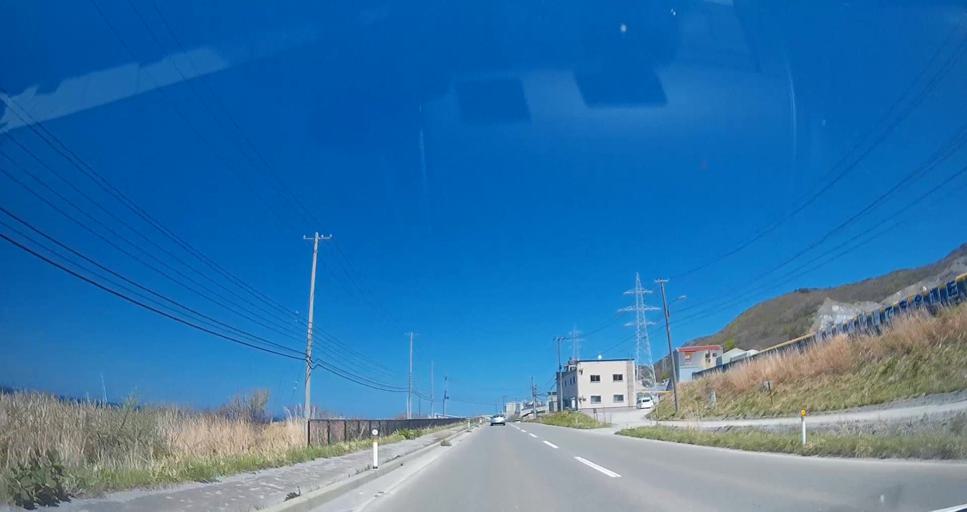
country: JP
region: Aomori
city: Mutsu
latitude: 41.4024
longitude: 141.4285
